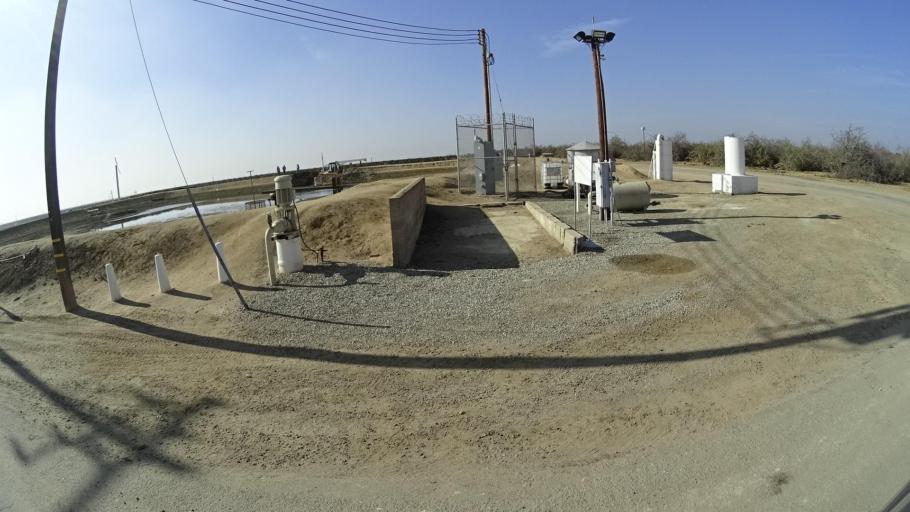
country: US
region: California
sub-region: Kern County
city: Shafter
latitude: 35.5440
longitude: -119.1334
